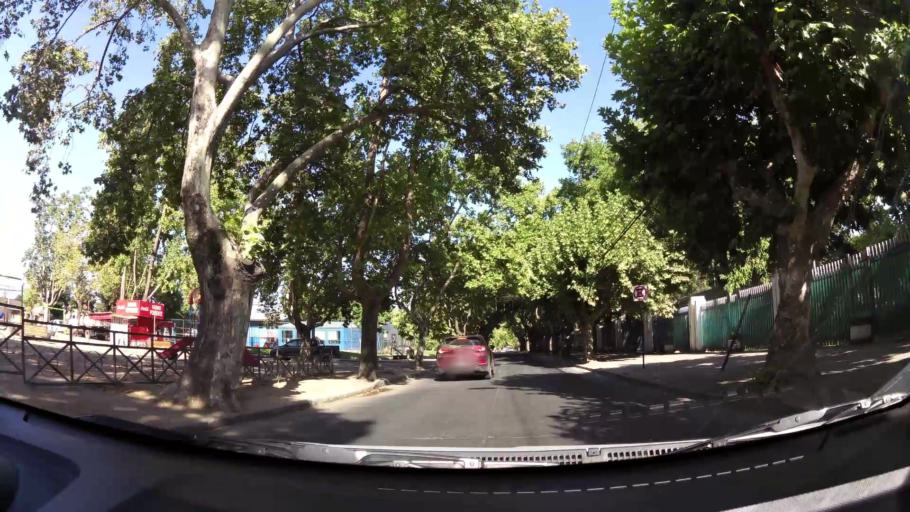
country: CL
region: Maule
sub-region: Provincia de Talca
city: Talca
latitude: -35.4212
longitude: -71.6714
